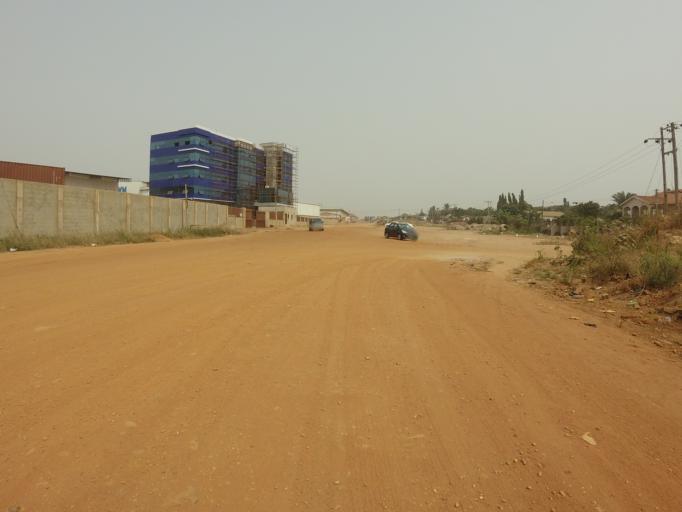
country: GH
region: Greater Accra
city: Nungua
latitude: 5.6467
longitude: -0.1008
